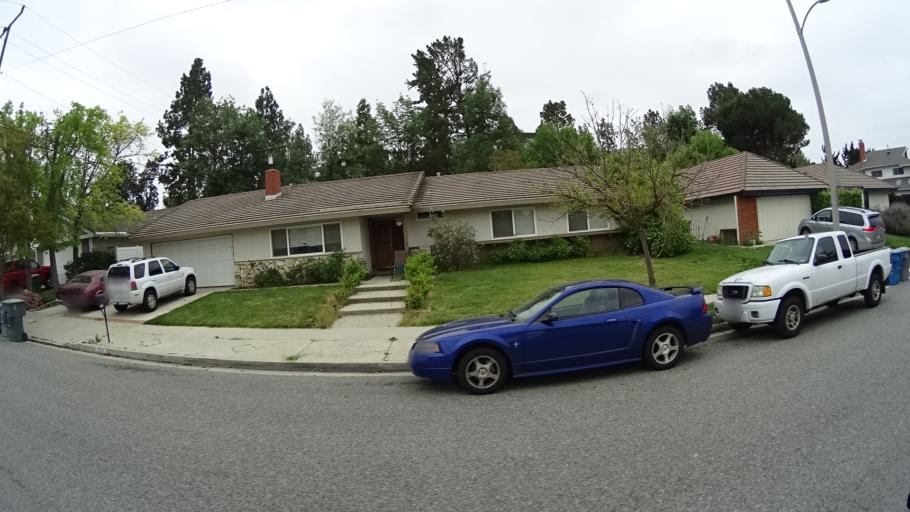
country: US
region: California
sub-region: Ventura County
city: Thousand Oaks
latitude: 34.2086
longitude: -118.8807
